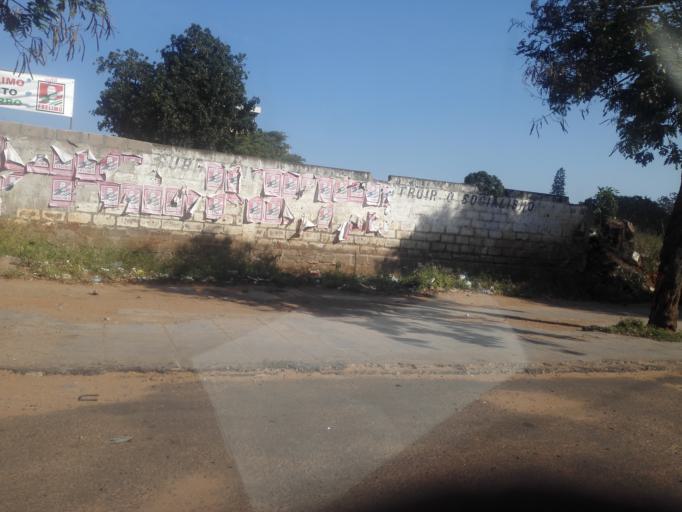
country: MZ
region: Maputo City
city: Maputo
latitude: -25.9543
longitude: 32.5877
